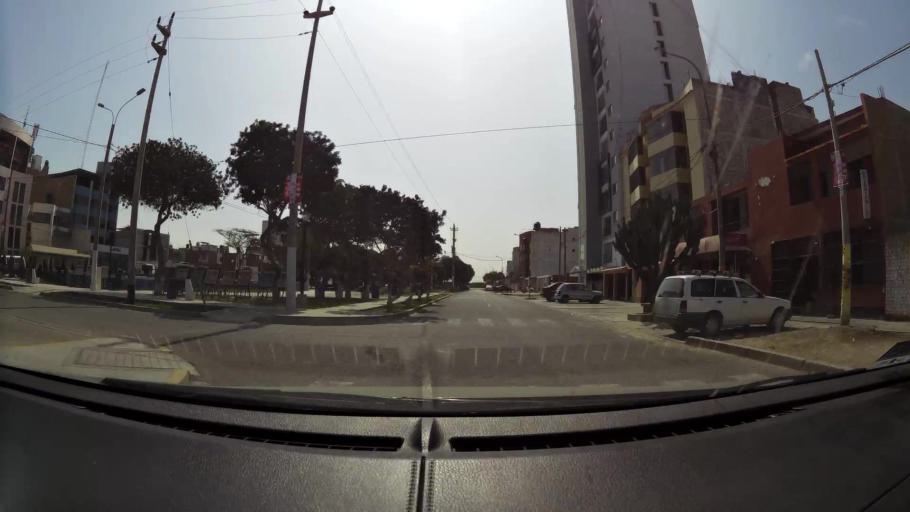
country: PE
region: La Libertad
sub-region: Provincia de Trujillo
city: Buenos Aires
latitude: -8.1294
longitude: -79.0462
